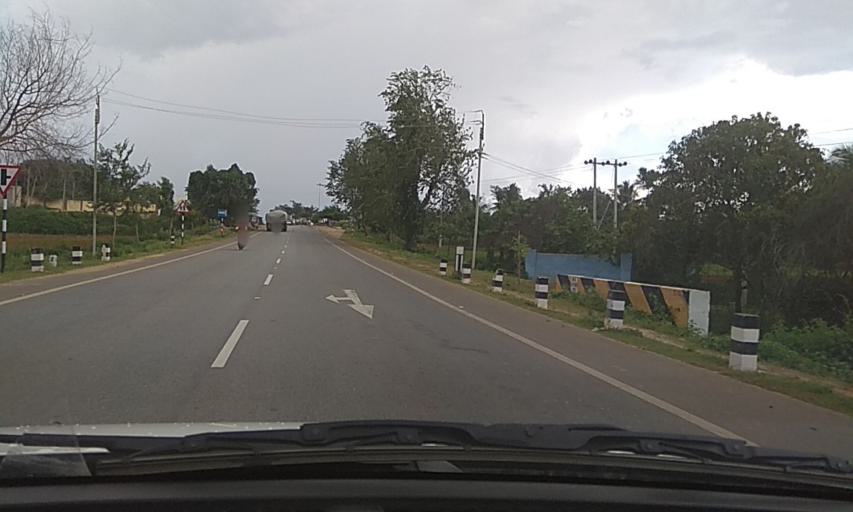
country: IN
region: Karnataka
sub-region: Tumkur
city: Kunigal
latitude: 12.8761
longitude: 77.0410
